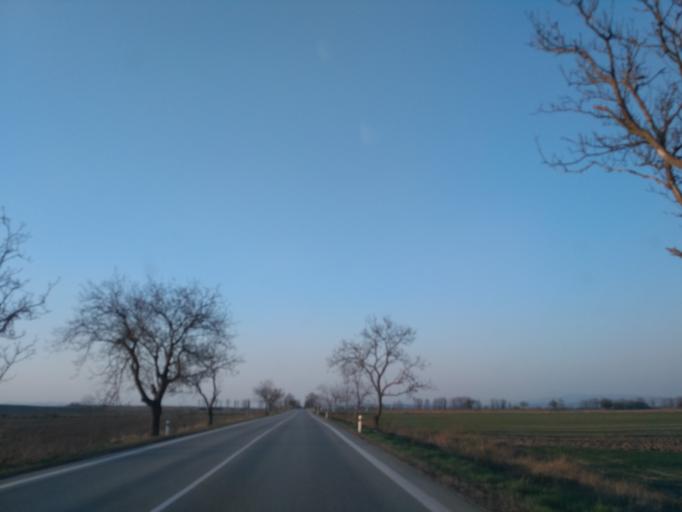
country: HU
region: Borsod-Abauj-Zemplen
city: Gonc
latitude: 48.5834
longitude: 21.2593
